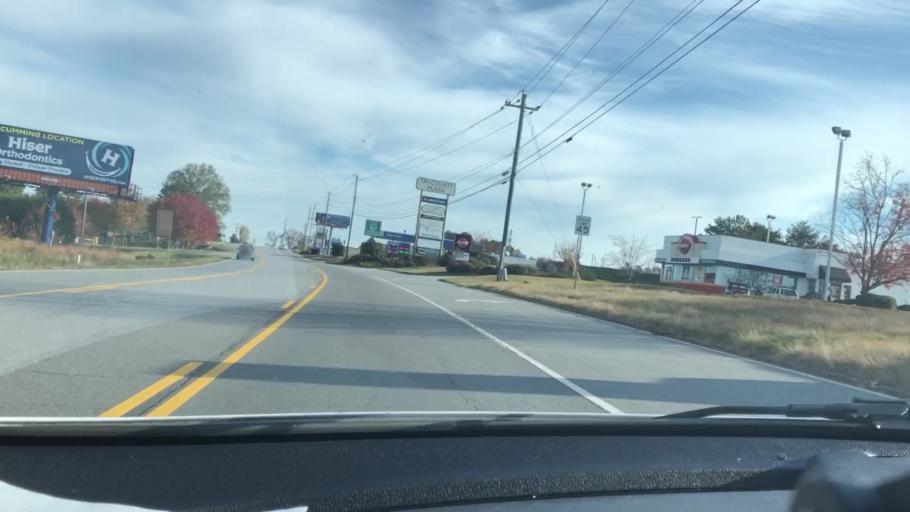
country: US
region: Georgia
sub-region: Forsyth County
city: Cumming
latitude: 34.1890
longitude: -84.1388
